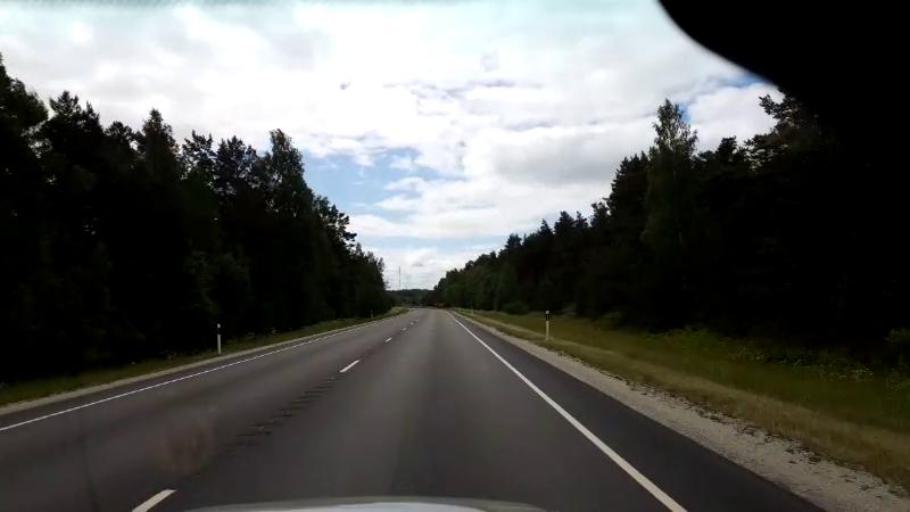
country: LV
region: Salacgrivas
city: Ainazi
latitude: 58.0898
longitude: 24.5079
